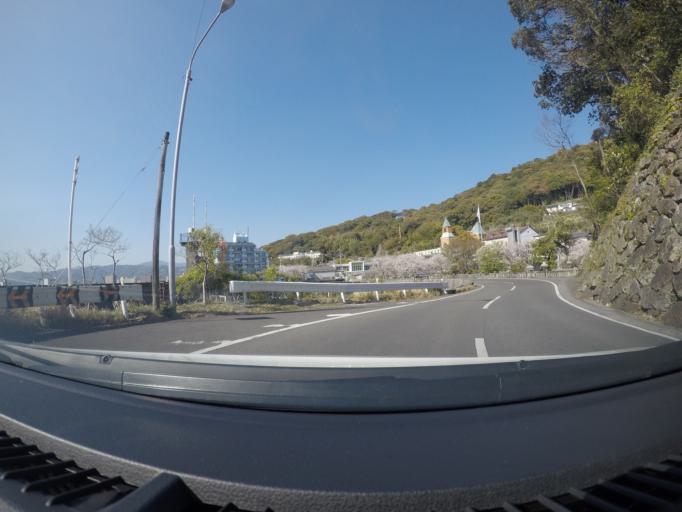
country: JP
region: Kochi
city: Kochi-shi
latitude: 33.5450
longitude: 133.5700
